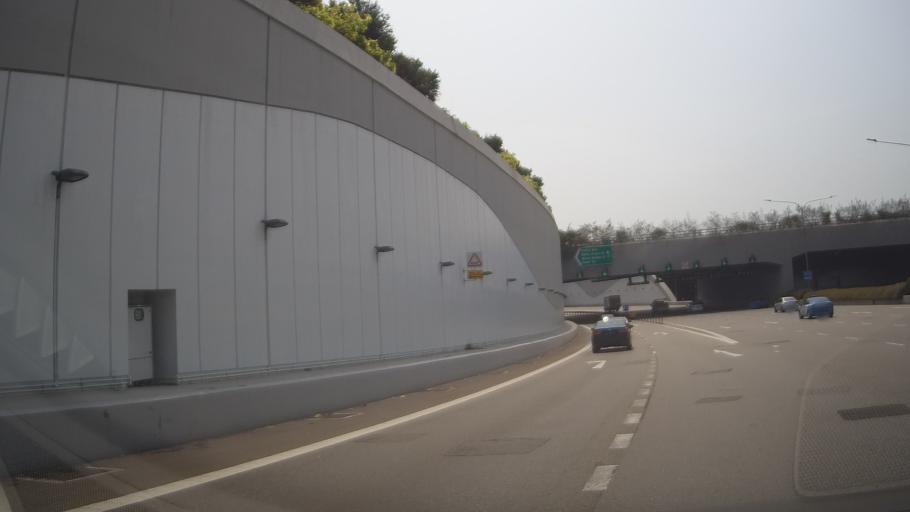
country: SG
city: Singapore
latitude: 1.2708
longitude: 103.8573
